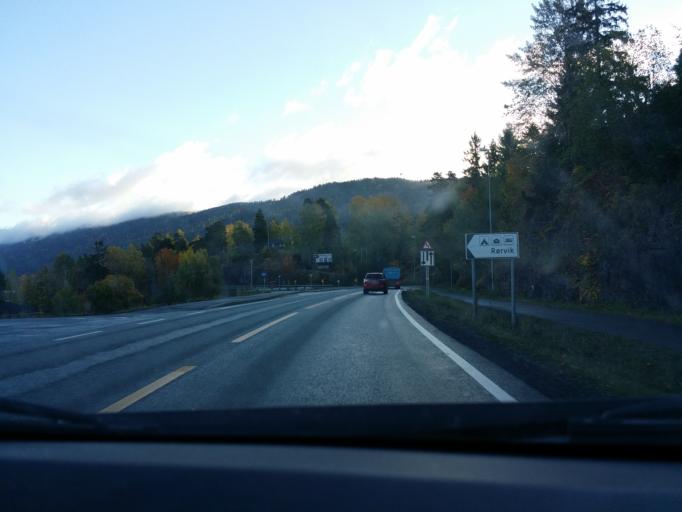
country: NO
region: Buskerud
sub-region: Hole
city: Vik
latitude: 60.0551
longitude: 10.2918
